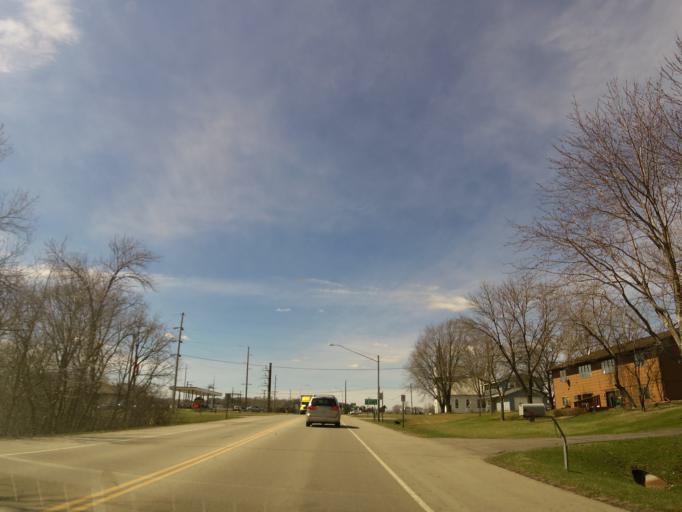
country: US
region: Minnesota
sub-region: Goodhue County
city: Cannon Falls
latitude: 44.5070
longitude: -92.9148
